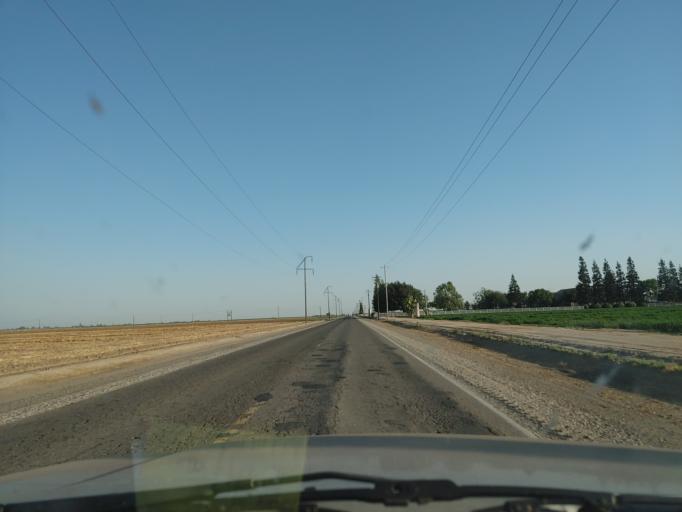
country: US
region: California
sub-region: Madera County
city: Chowchilla
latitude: 37.1618
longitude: -120.3831
